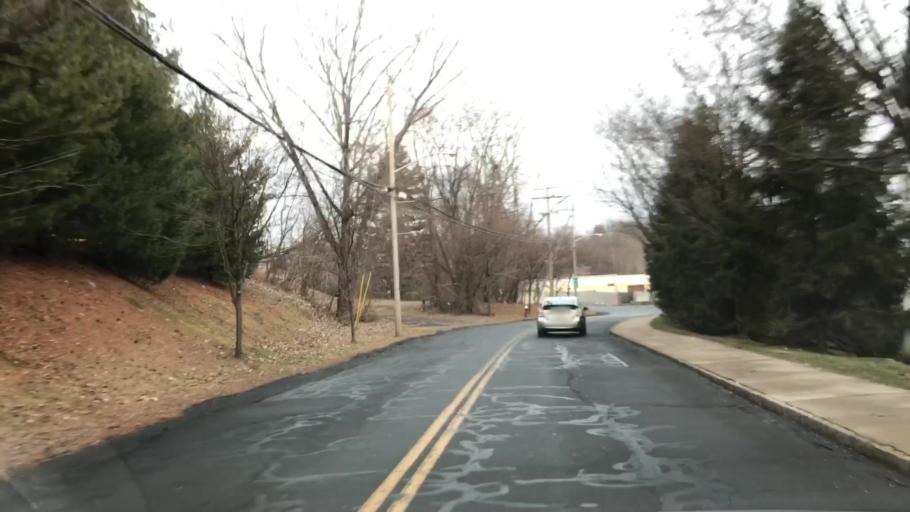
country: US
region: New York
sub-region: Rockland County
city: Haverstraw
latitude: 41.1904
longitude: -73.9601
